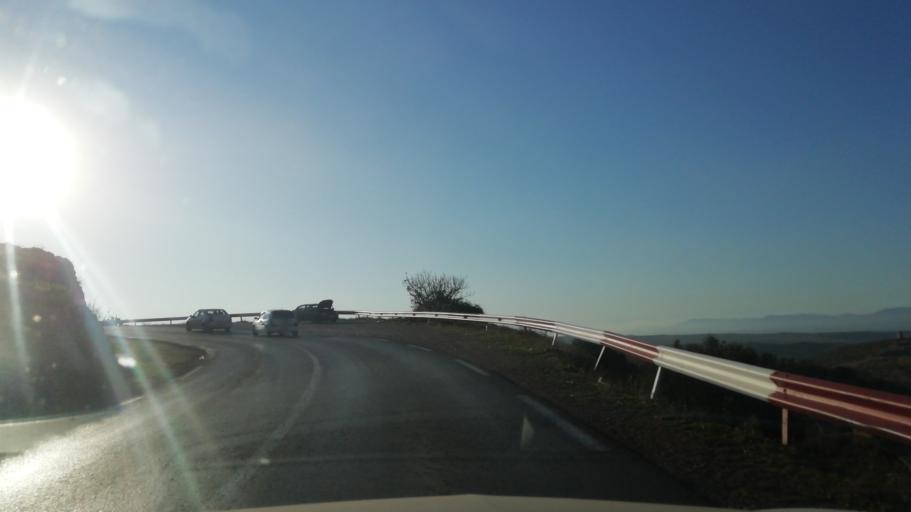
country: DZ
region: Tlemcen
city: Beni Mester
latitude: 34.8564
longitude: -1.4483
